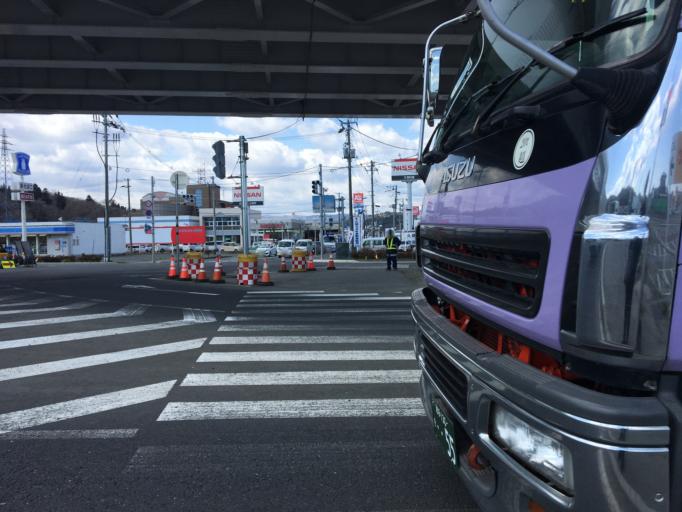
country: JP
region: Aomori
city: Hachinohe
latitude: 40.1891
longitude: 141.7881
